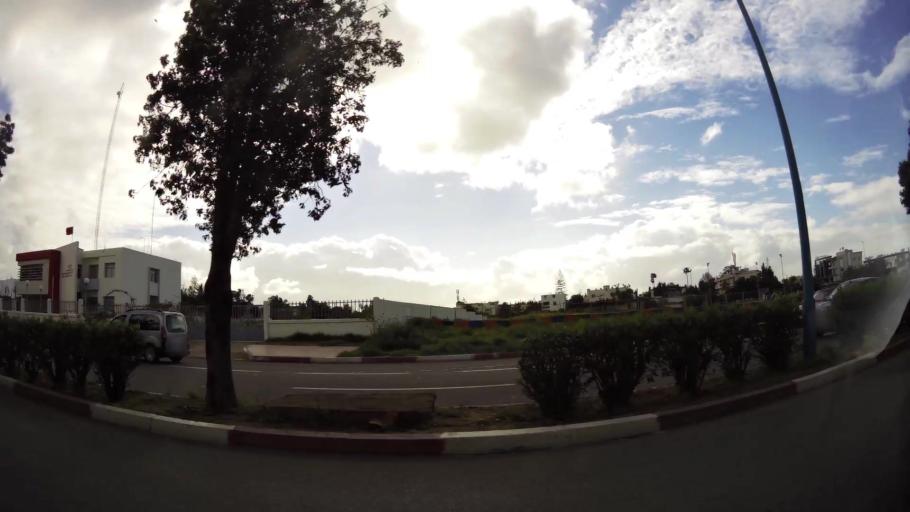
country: MA
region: Grand Casablanca
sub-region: Casablanca
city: Casablanca
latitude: 33.5485
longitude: -7.6223
